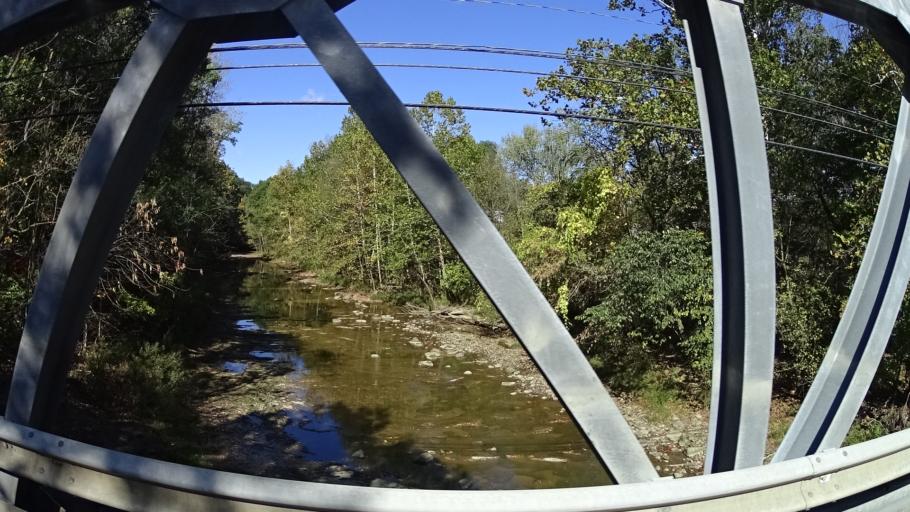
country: US
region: Ohio
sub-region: Lorain County
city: Grafton
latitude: 41.2746
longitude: -82.0667
